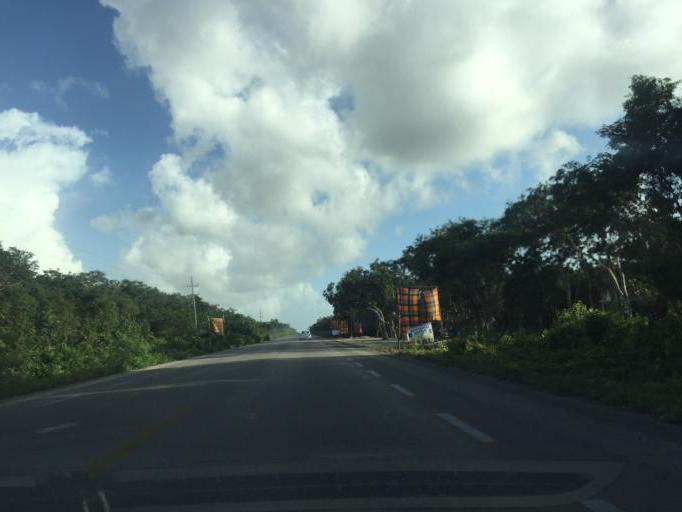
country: MX
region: Quintana Roo
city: Coba
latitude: 20.4670
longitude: -87.6837
